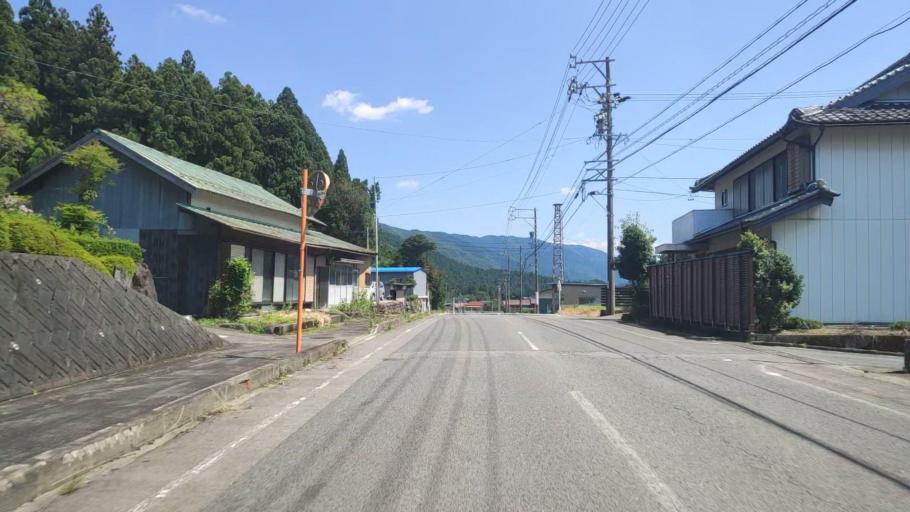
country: JP
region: Gifu
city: Godo
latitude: 35.6515
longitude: 136.5952
